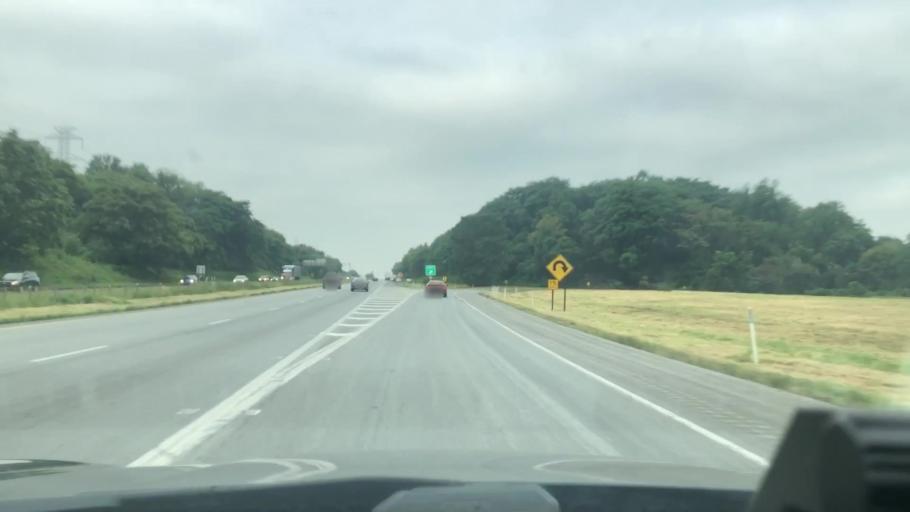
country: US
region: Pennsylvania
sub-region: Berks County
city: Temple
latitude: 40.4112
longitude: -75.9393
